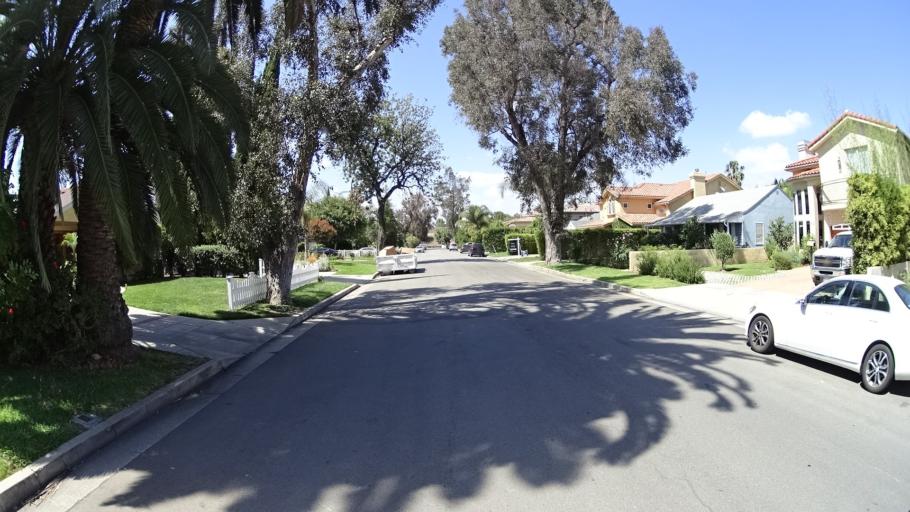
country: US
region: California
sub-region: Los Angeles County
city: Sherman Oaks
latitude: 34.1533
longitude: -118.4444
